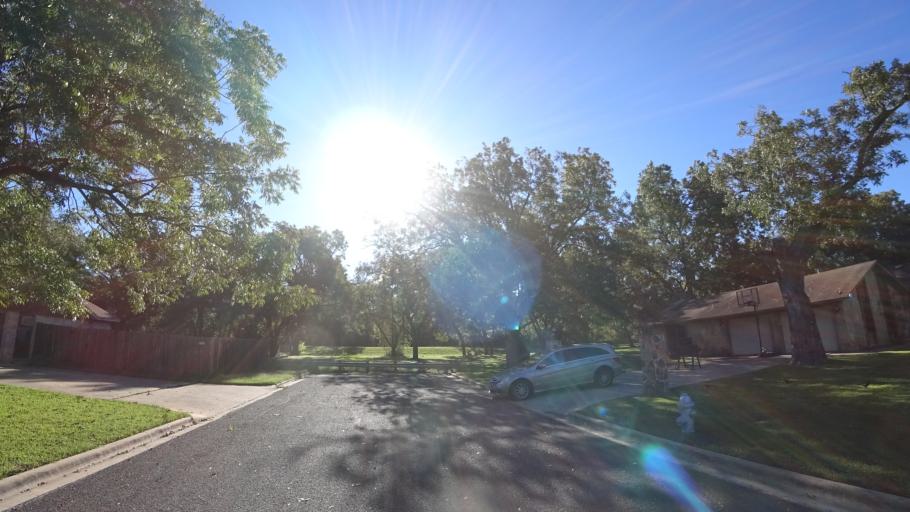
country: US
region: Texas
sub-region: Travis County
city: Hornsby Bend
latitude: 30.3104
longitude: -97.6513
